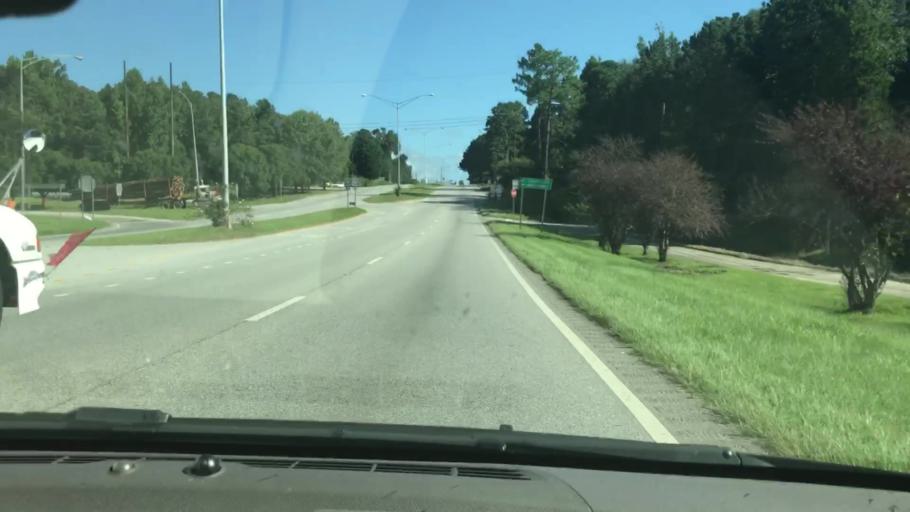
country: US
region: Alabama
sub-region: Barbour County
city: Eufaula
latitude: 31.9110
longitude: -85.1488
